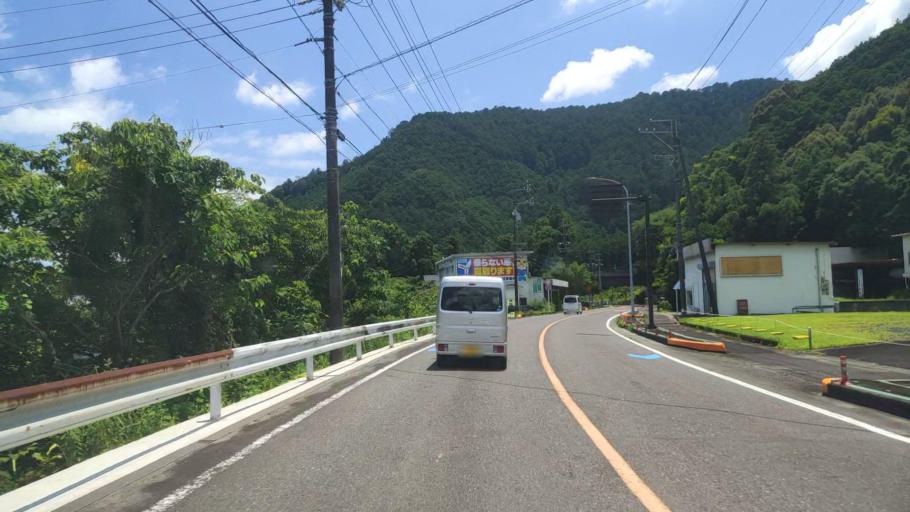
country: JP
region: Mie
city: Owase
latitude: 34.1176
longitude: 136.2196
